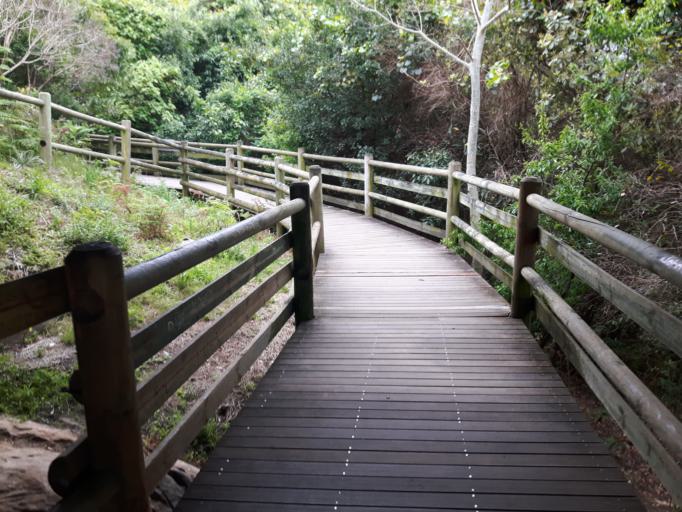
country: ZA
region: Eastern Cape
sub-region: Cacadu District Municipality
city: Kareedouw
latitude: -33.9684
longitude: 23.9308
